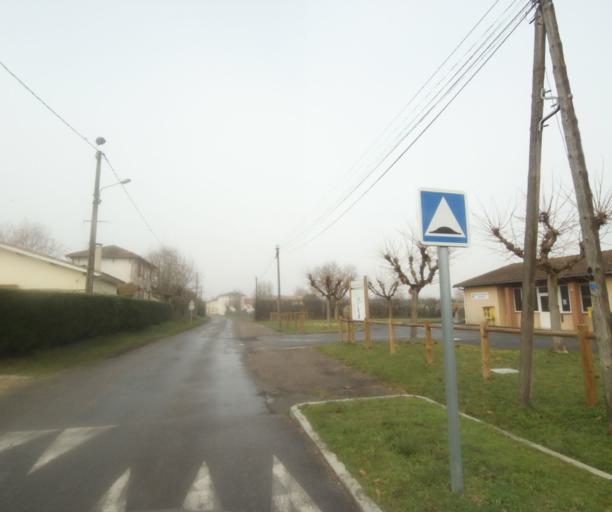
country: FR
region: Midi-Pyrenees
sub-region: Departement de la Haute-Garonne
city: Villaudric
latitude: 43.8367
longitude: 1.4632
